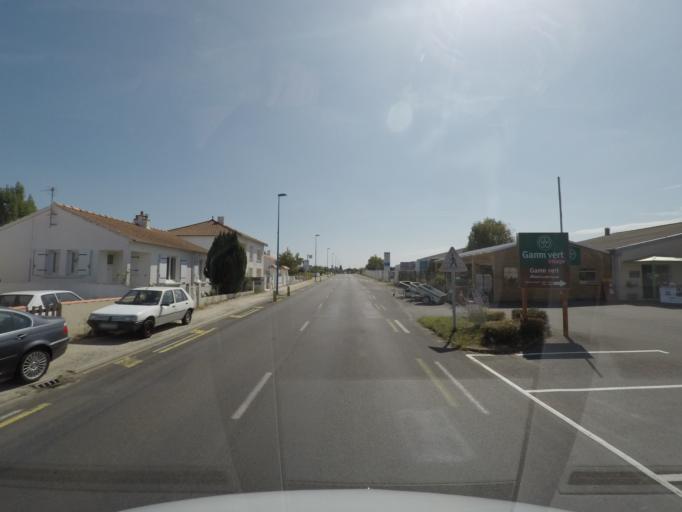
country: FR
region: Pays de la Loire
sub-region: Departement de la Vendee
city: Beauvoir-sur-Mer
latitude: 46.9106
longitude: -2.0343
